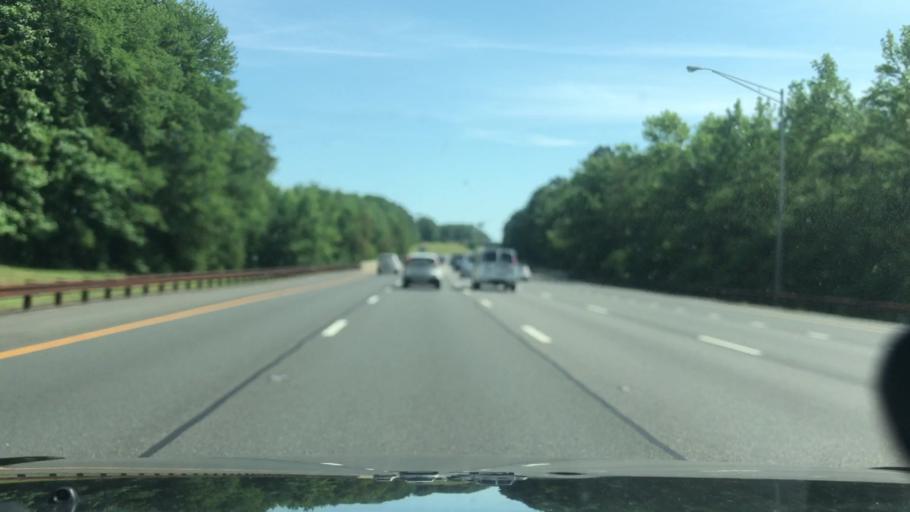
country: US
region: New Jersey
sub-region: Monmouth County
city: Shark River Hills
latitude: 40.2097
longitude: -74.0985
